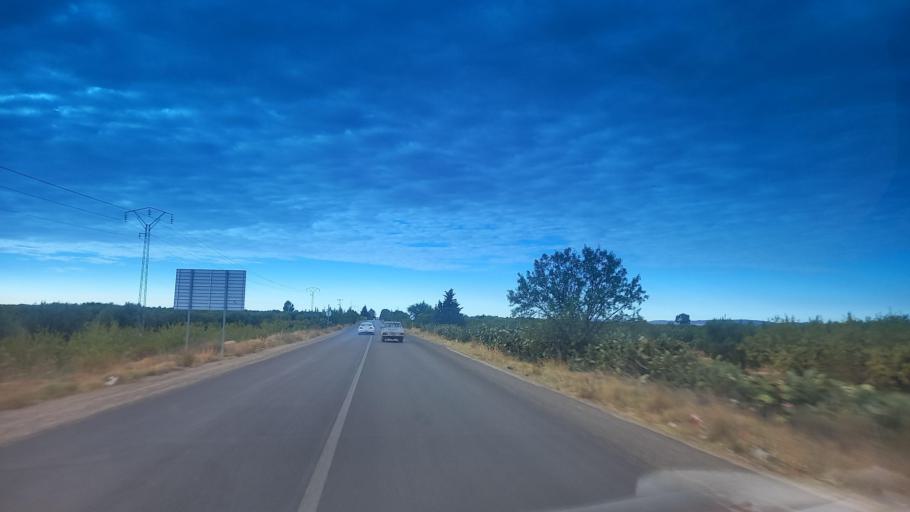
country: TN
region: Al Qasrayn
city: Sbiba
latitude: 35.3069
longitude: 9.0865
